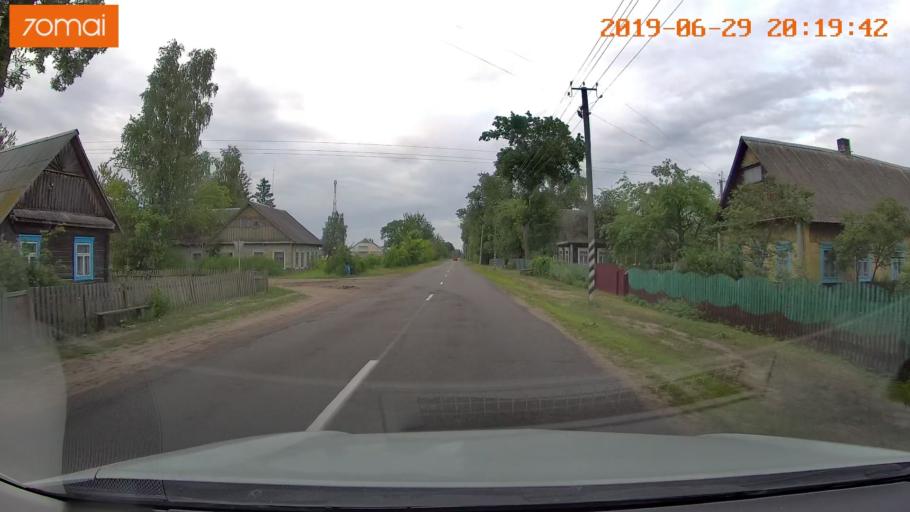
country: BY
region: Brest
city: Asnyezhytsy
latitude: 52.4036
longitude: 26.2457
